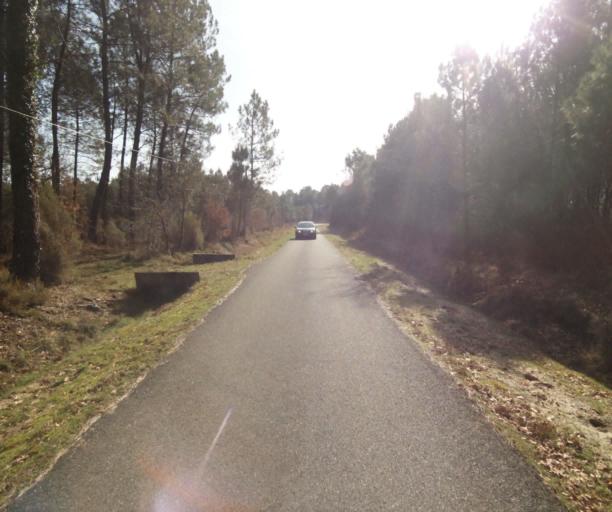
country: FR
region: Aquitaine
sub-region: Departement des Landes
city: Roquefort
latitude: 44.2178
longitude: -0.2445
